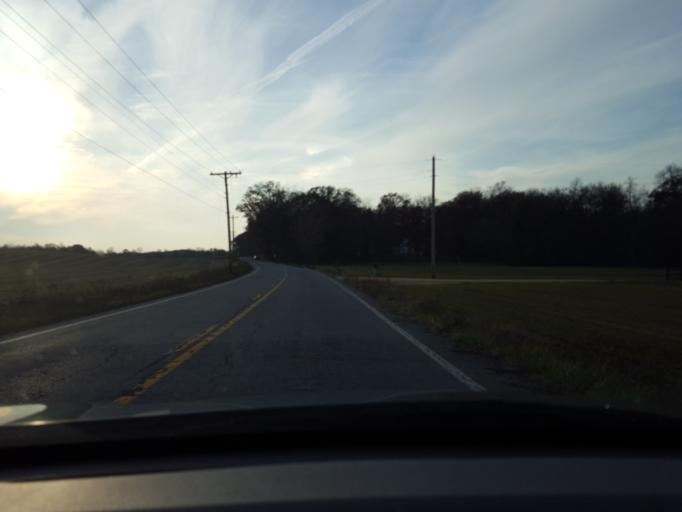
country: US
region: Maryland
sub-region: Charles County
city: Hughesville
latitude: 38.5320
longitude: -76.7896
